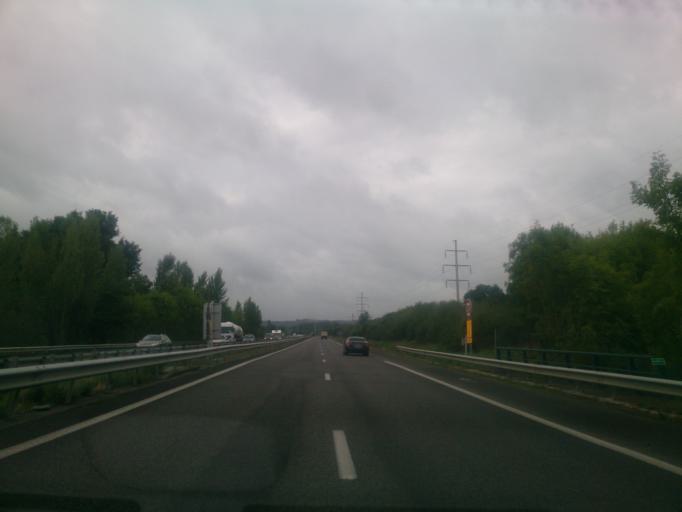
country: FR
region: Midi-Pyrenees
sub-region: Departement de la Haute-Garonne
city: Martres-Tolosane
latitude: 43.1946
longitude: 0.9912
